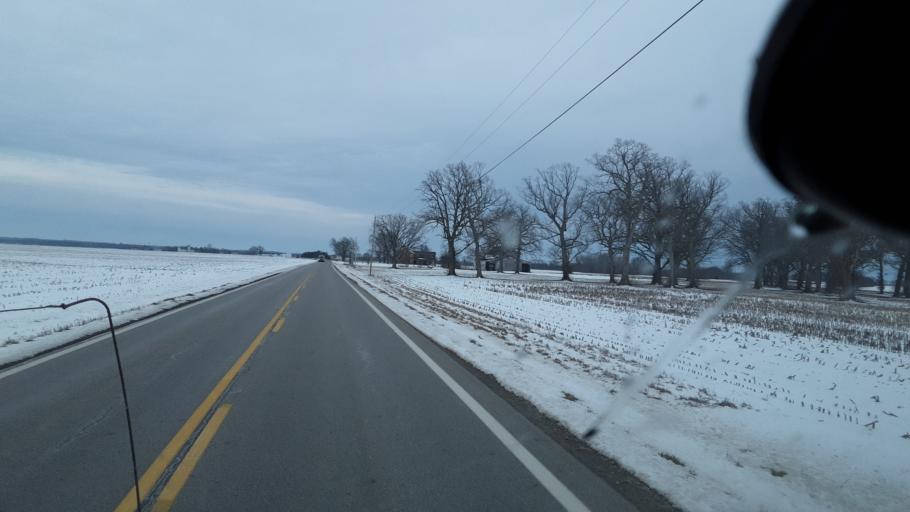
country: US
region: Ohio
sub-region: Pickaway County
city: Circleville
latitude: 39.6192
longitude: -83.0186
